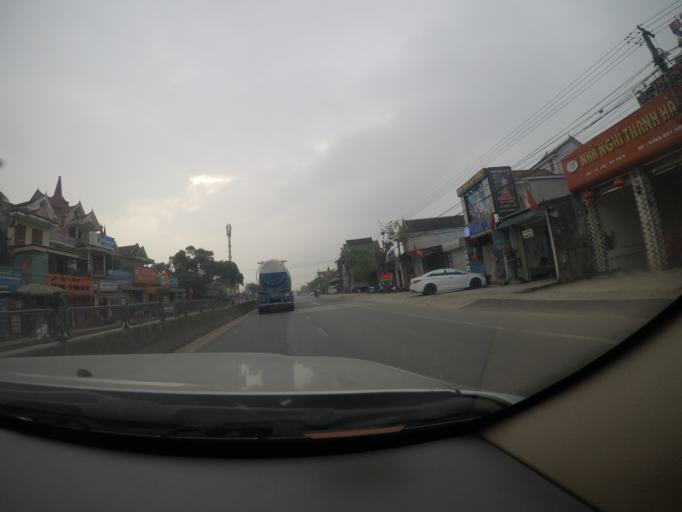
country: VN
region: Ha Tinh
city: Cam Xuyen
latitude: 18.1985
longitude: 106.1666
